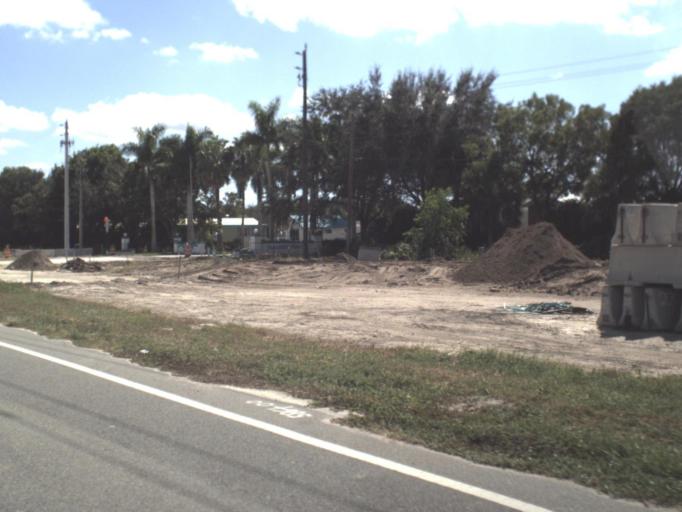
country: US
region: Florida
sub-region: Collier County
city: Lely Resort
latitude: 26.0416
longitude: -81.6653
